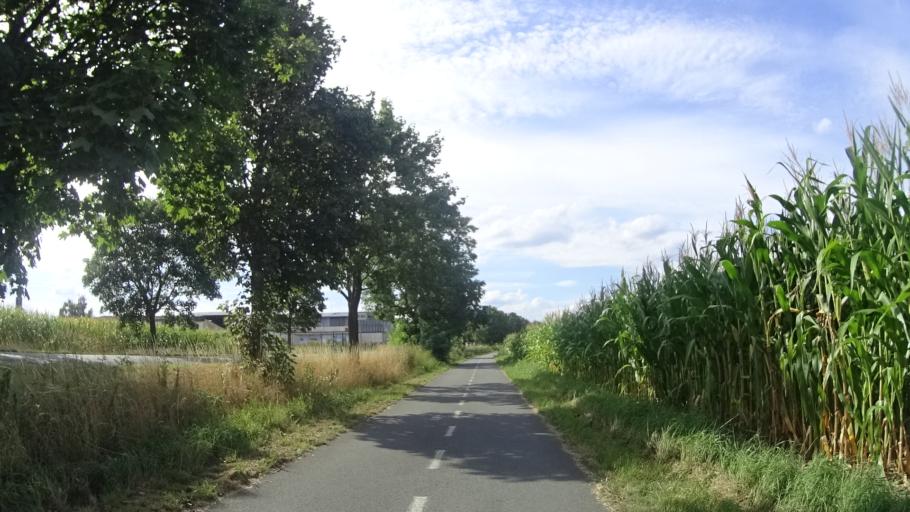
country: CZ
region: Olomoucky
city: Moravicany
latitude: 49.7703
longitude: 16.9442
